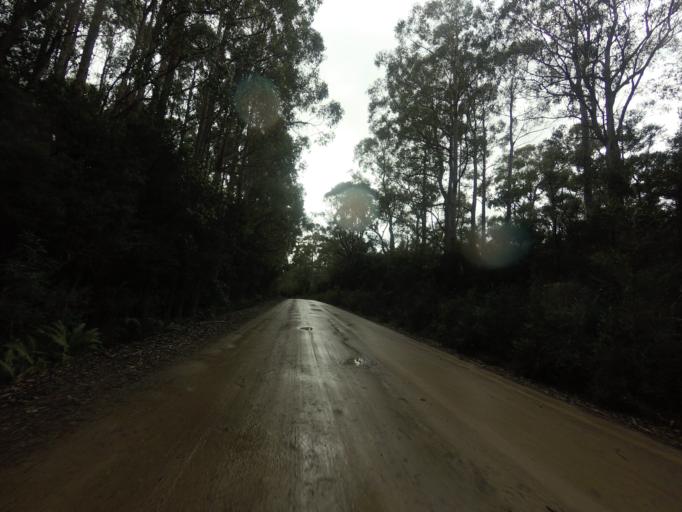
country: AU
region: Tasmania
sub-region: Huon Valley
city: Geeveston
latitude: -43.4577
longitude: 146.9020
